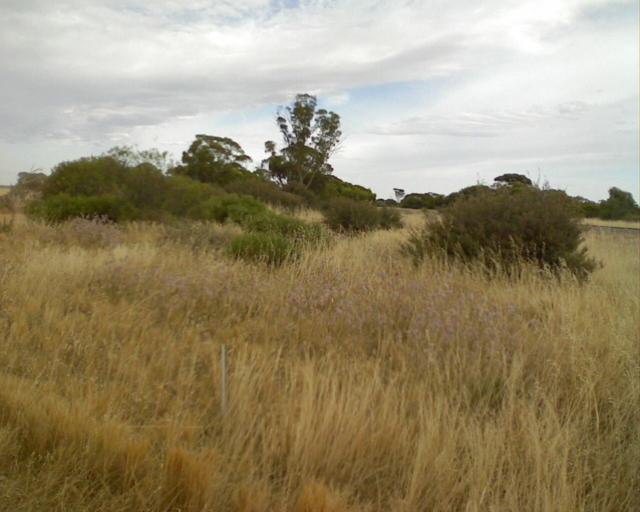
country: AU
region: Western Australia
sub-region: Moora
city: Moora
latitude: -29.7754
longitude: 115.9309
